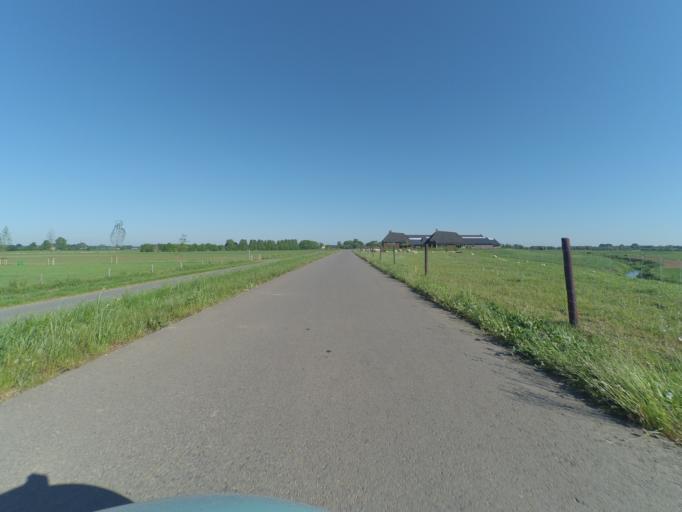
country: NL
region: Gelderland
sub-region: Gemeente Voorst
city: Voorst
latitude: 52.1676
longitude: 6.1733
